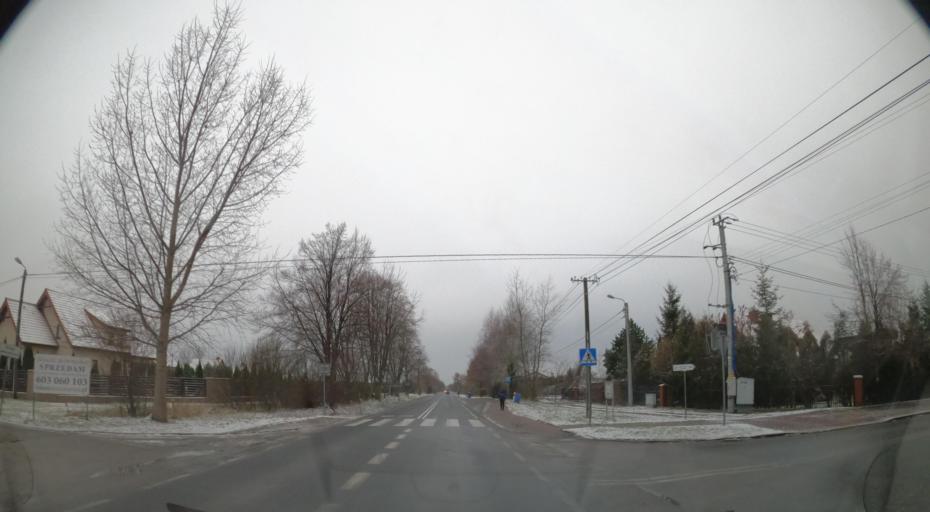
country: PL
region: Masovian Voivodeship
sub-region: Powiat plocki
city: Maszewo Duze
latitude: 52.5712
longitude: 19.6060
